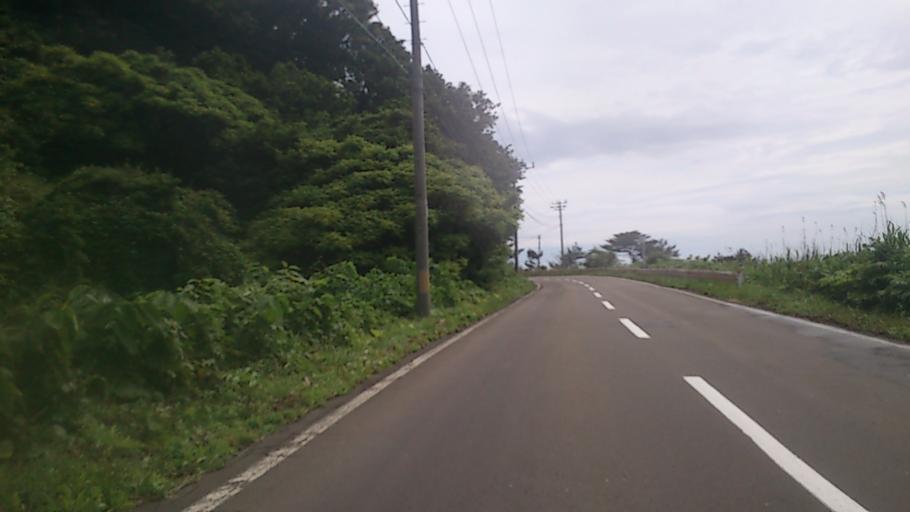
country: JP
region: Akita
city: Noshiromachi
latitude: 40.4694
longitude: 139.9463
